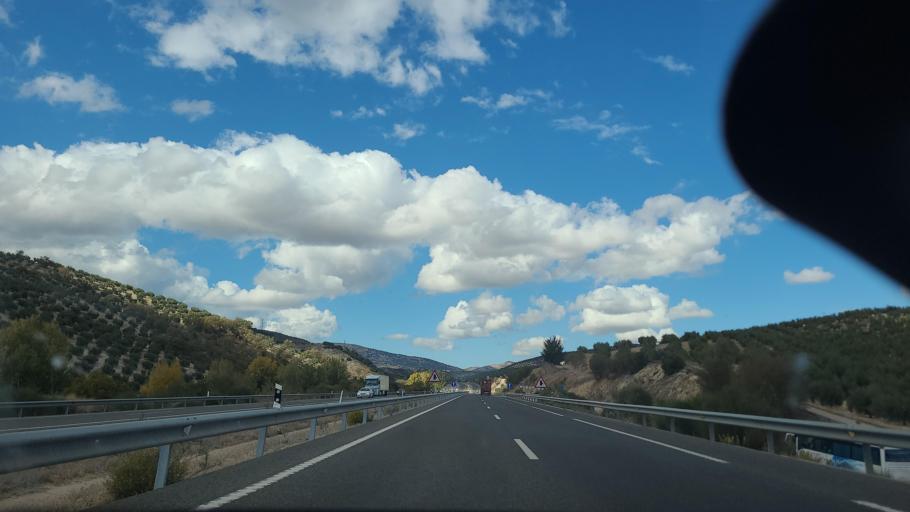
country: ES
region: Andalusia
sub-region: Provincia de Granada
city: Campotejar
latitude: 37.4956
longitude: -3.6249
